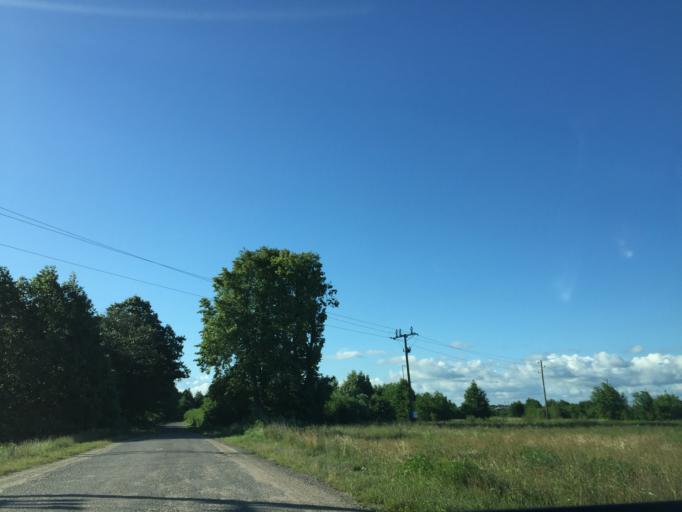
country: LV
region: Ventspils
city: Ventspils
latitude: 57.4081
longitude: 21.6453
